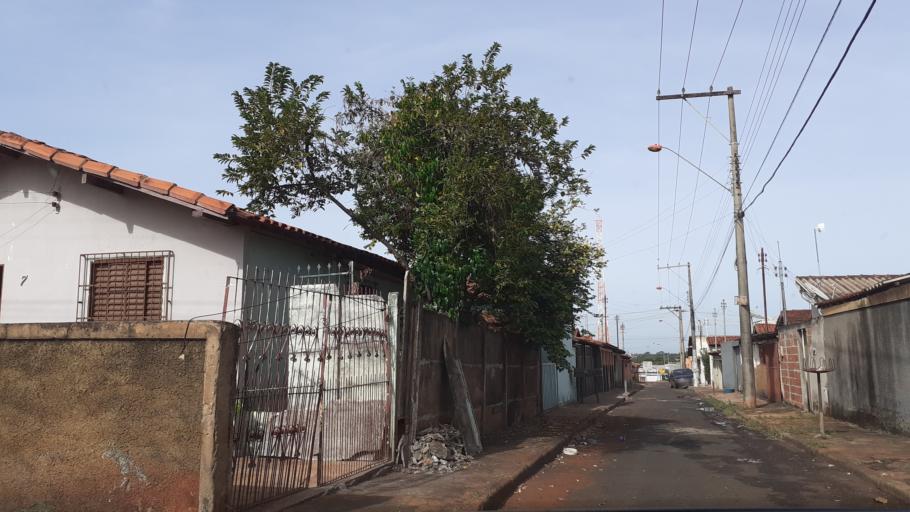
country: BR
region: Goias
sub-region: Itumbiara
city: Itumbiara
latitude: -18.4166
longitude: -49.2367
